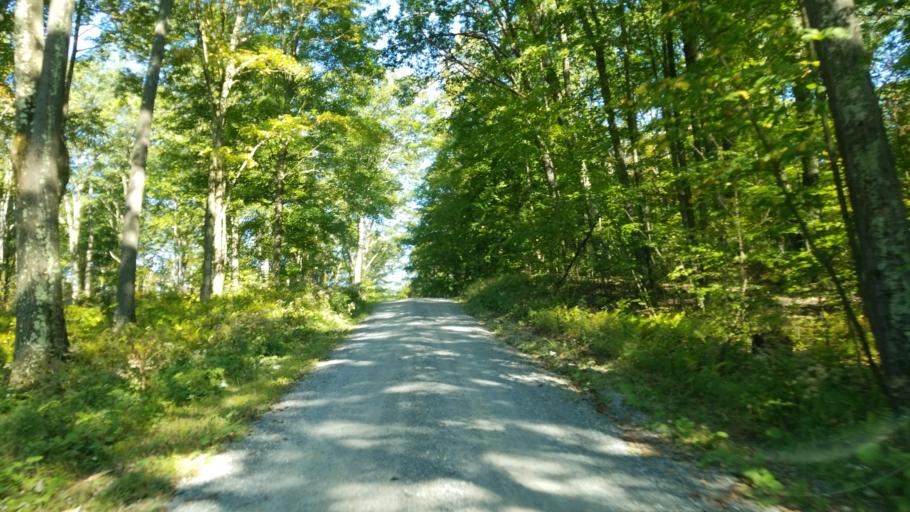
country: US
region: Pennsylvania
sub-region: Clearfield County
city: Treasure Lake
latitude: 41.1397
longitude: -78.5727
